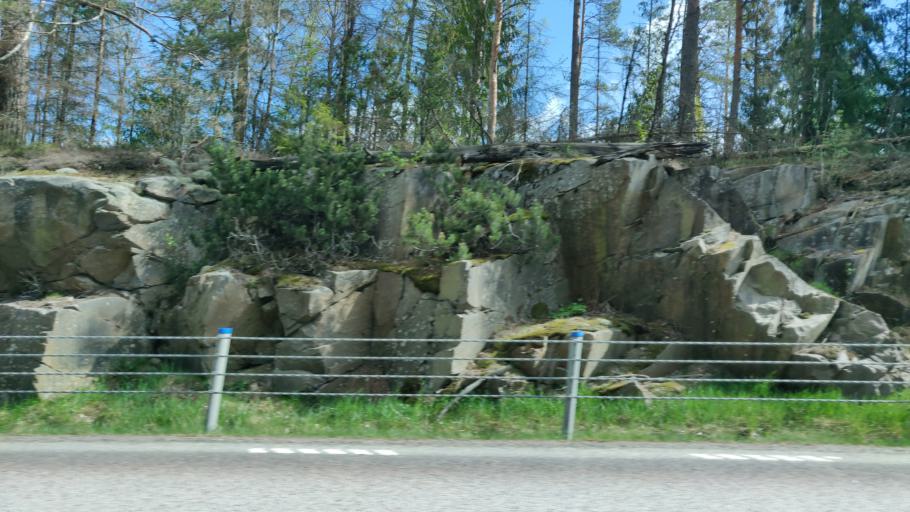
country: SE
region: Vaermland
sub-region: Karlstads Kommun
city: Molkom
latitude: 59.5355
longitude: 13.6187
